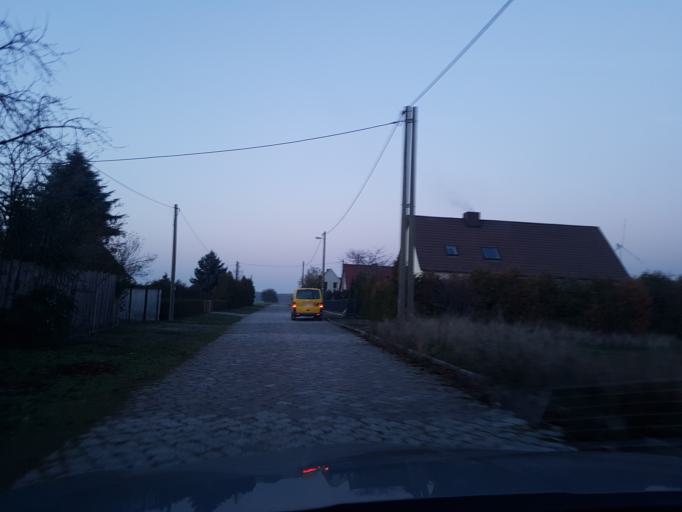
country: DE
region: Saxony
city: Arzberg
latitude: 51.5503
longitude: 13.1576
